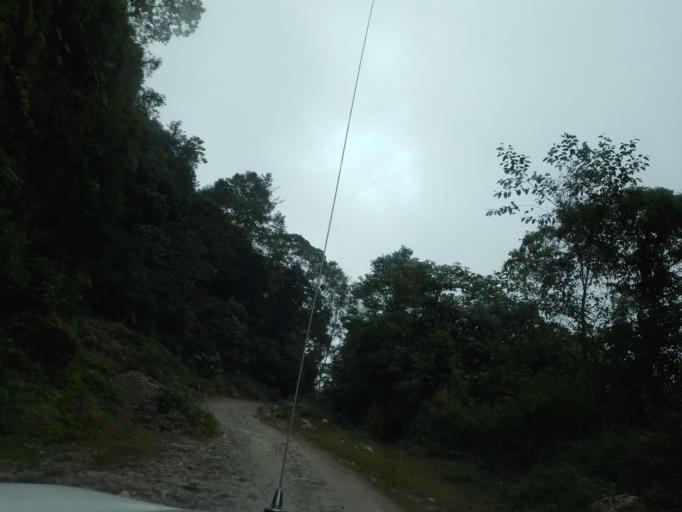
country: MX
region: Chiapas
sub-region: Union Juarez
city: Santo Domingo
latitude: 15.0919
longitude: -92.0923
